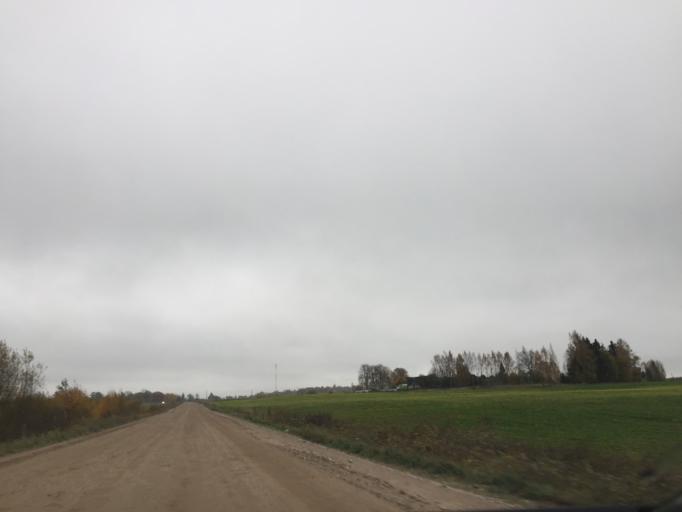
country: LV
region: Sigulda
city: Sigulda
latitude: 57.2713
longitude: 24.8528
